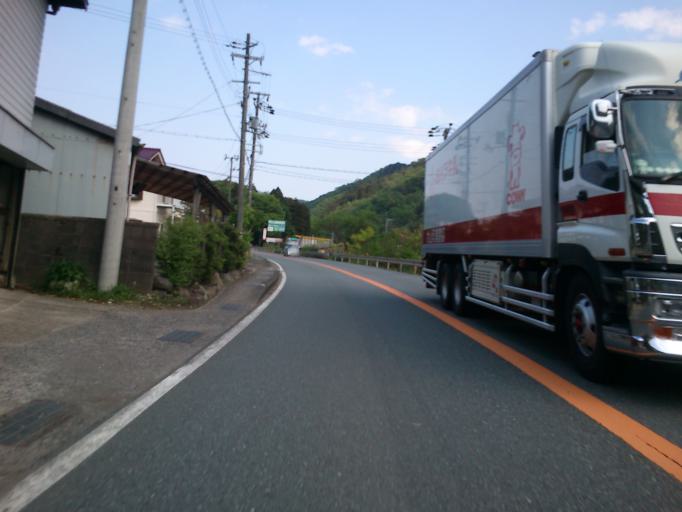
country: JP
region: Kyoto
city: Fukuchiyama
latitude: 35.3246
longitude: 134.9683
